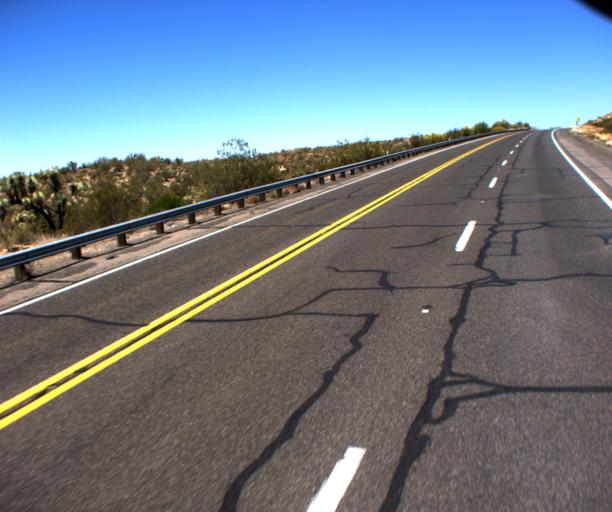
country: US
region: Arizona
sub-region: Yavapai County
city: Congress
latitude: 34.2209
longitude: -113.0687
